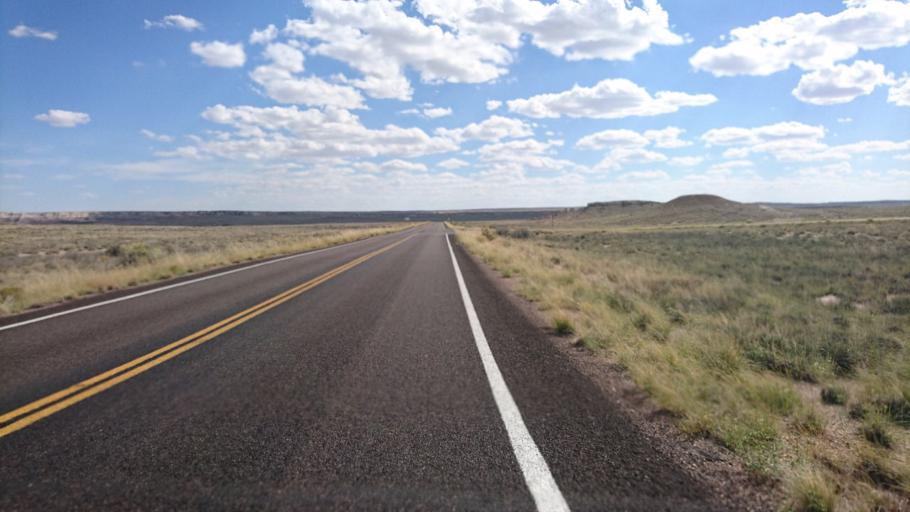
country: US
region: Arizona
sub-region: Navajo County
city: Holbrook
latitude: 34.8883
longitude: -109.8027
